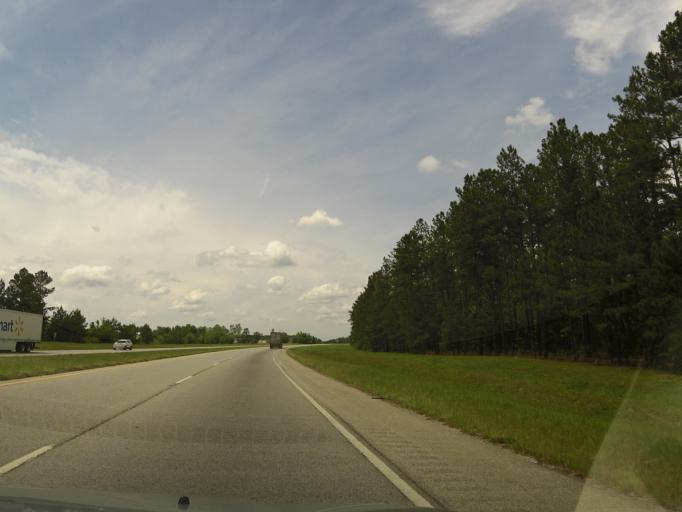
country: US
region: Georgia
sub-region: Emanuel County
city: Swainsboro
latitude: 32.5968
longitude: -82.3752
